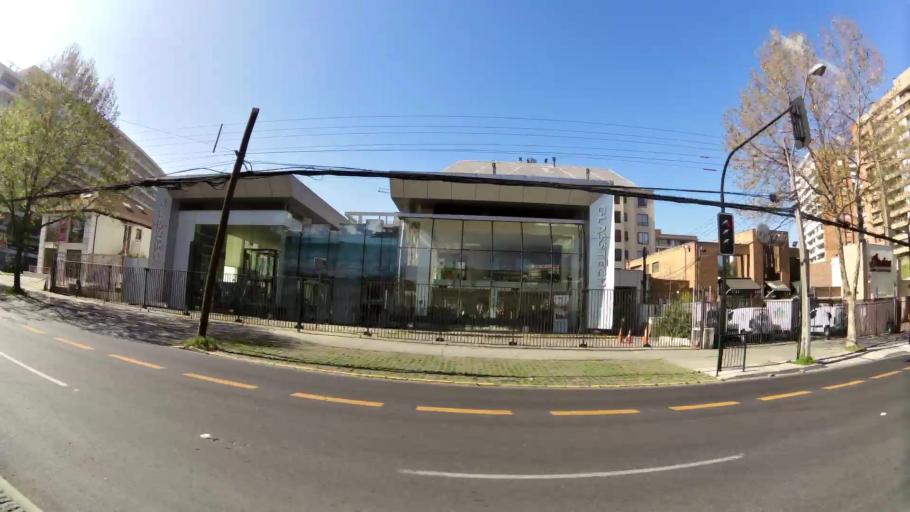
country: CL
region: Santiago Metropolitan
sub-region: Provincia de Santiago
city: Villa Presidente Frei, Nunoa, Santiago, Chile
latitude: -33.4060
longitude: -70.5595
